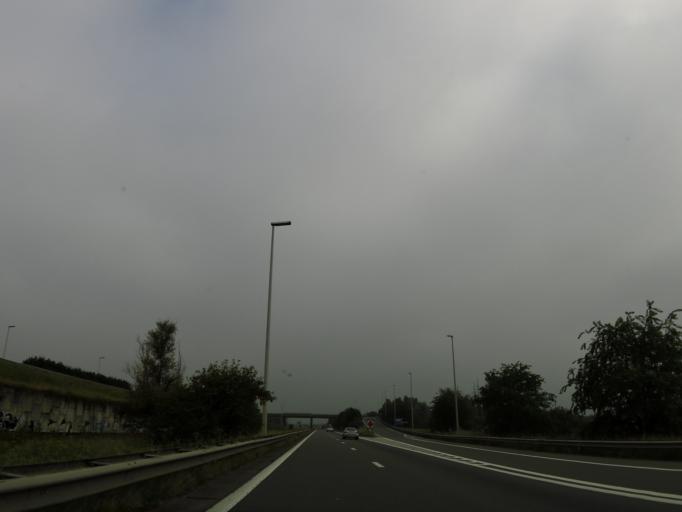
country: BE
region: Flanders
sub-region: Provincie Antwerpen
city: Stabroek
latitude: 51.3227
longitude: 4.3511
